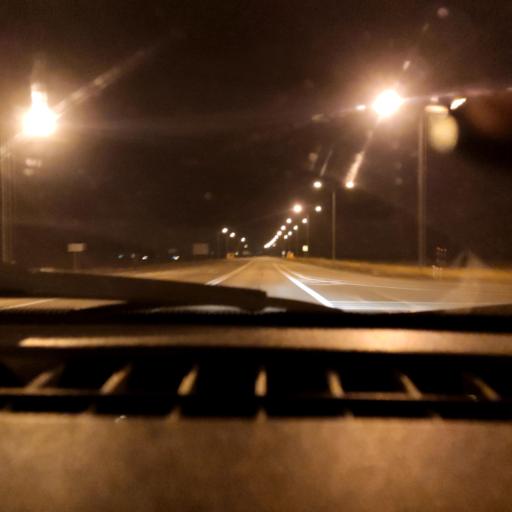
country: RU
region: Bashkortostan
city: Kushnarenkovo
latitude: 55.0642
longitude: 55.4215
